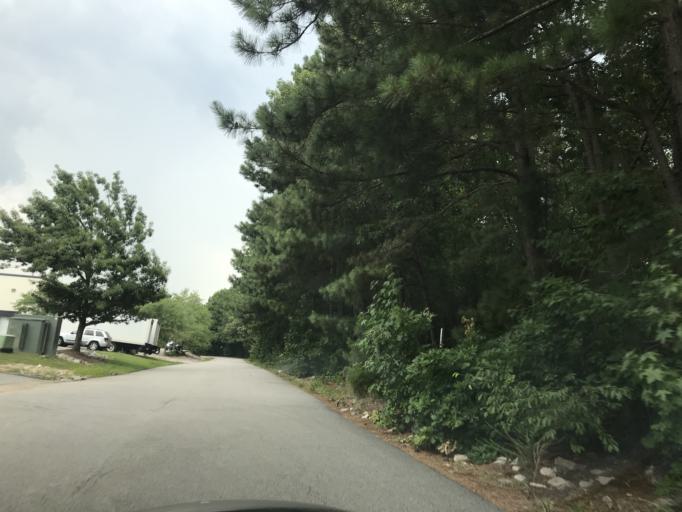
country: US
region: North Carolina
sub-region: Wake County
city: Wake Forest
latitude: 35.8892
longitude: -78.5807
